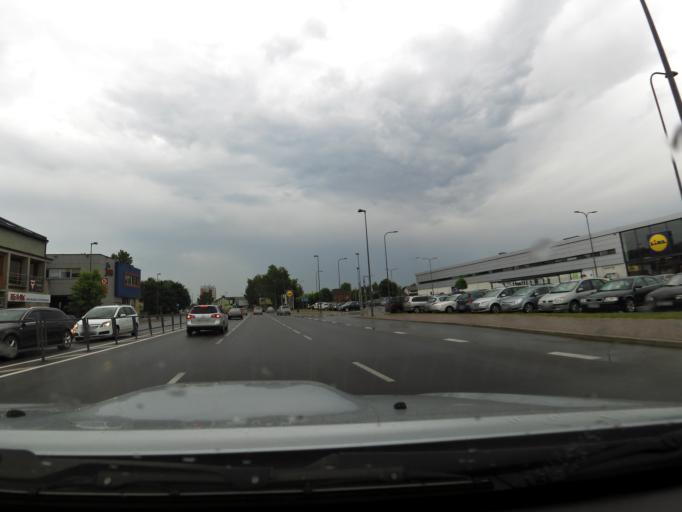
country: LT
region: Marijampoles apskritis
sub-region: Marijampole Municipality
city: Marijampole
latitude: 54.5564
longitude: 23.3546
